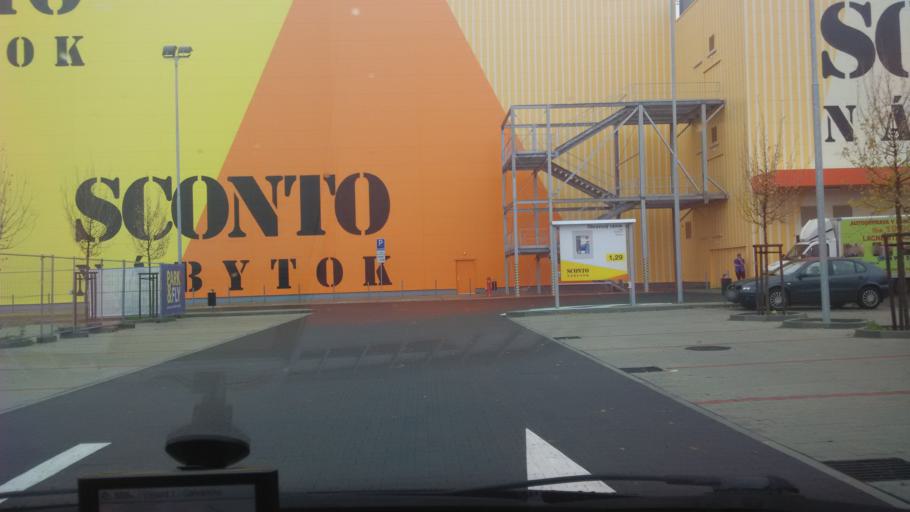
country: SK
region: Bratislavsky
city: Bratislava
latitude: 48.1635
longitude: 17.1856
